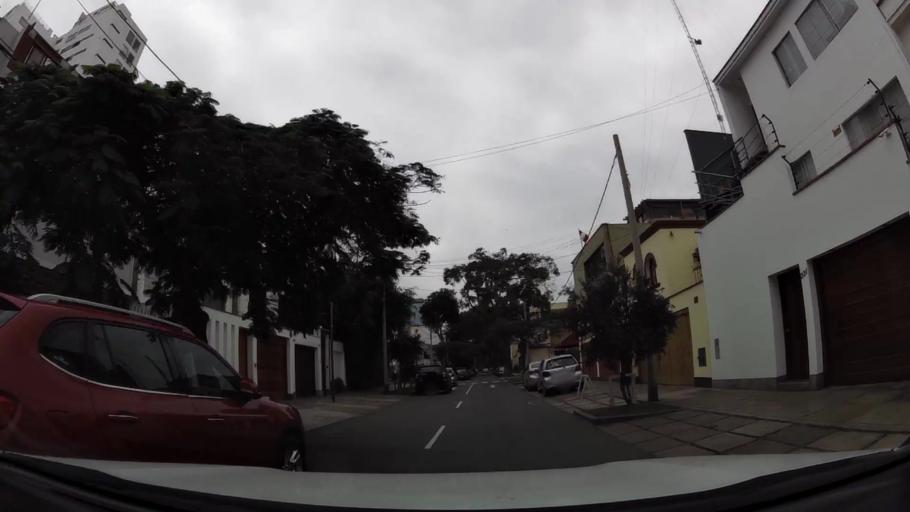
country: PE
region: Lima
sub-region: Lima
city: Surco
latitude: -12.1285
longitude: -77.0220
